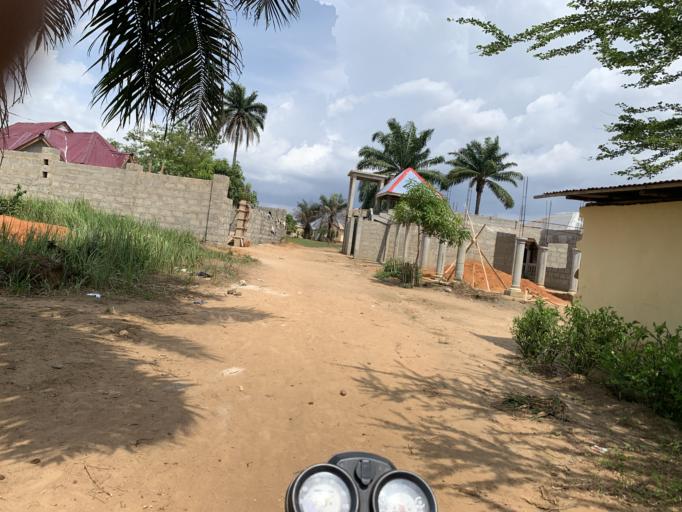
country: SL
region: Western Area
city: Waterloo
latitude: 8.3621
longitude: -13.0435
